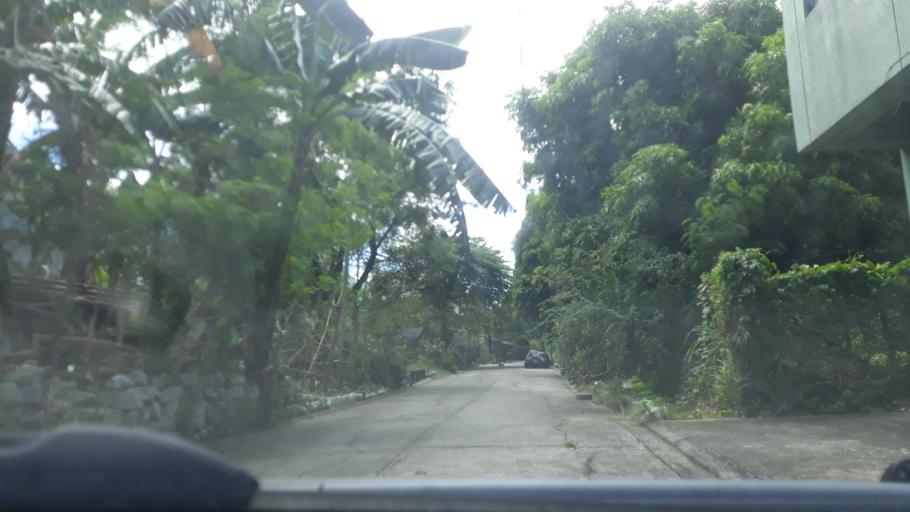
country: PH
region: Calabarzon
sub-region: Province of Cavite
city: Dasmarinas
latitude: 14.3245
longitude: 120.9499
